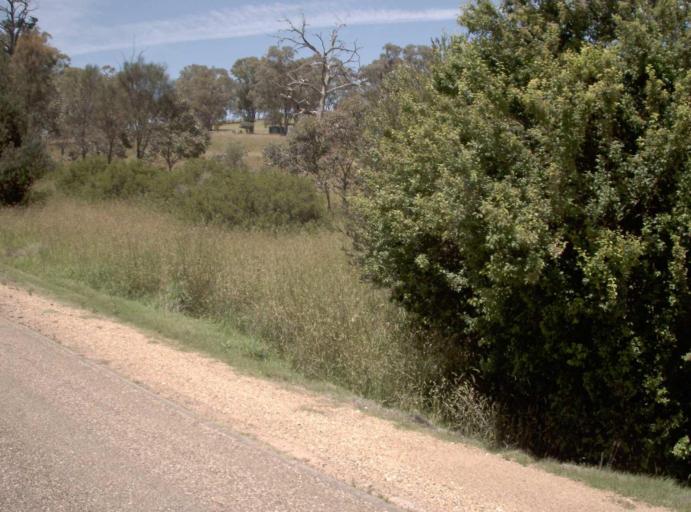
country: AU
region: Victoria
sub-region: East Gippsland
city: Bairnsdale
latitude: -37.3614
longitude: 147.8229
